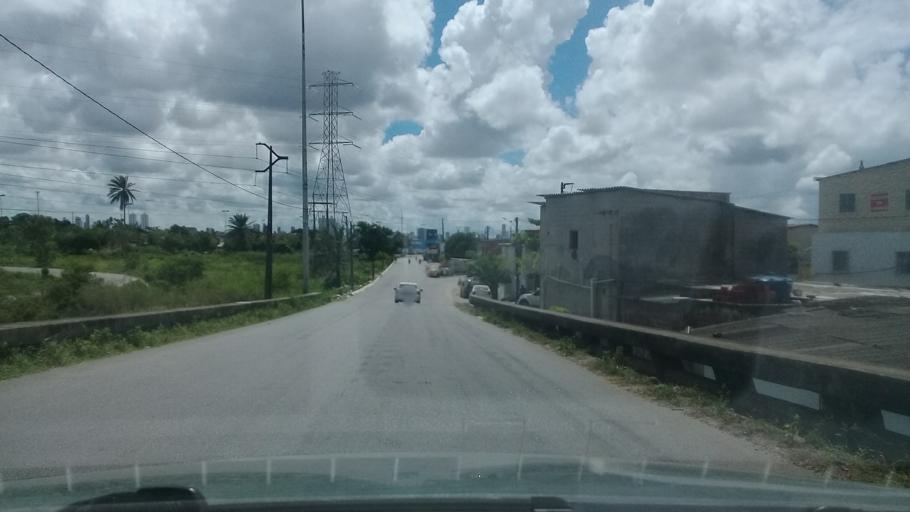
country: BR
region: Pernambuco
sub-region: Recife
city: Recife
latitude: -8.0679
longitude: -34.9403
